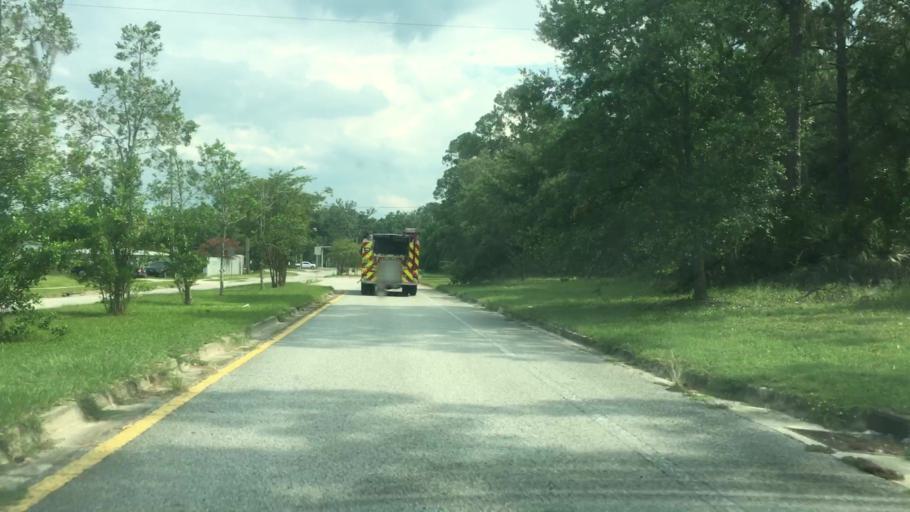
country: US
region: Florida
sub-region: Duval County
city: Neptune Beach
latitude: 30.2895
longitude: -81.5050
